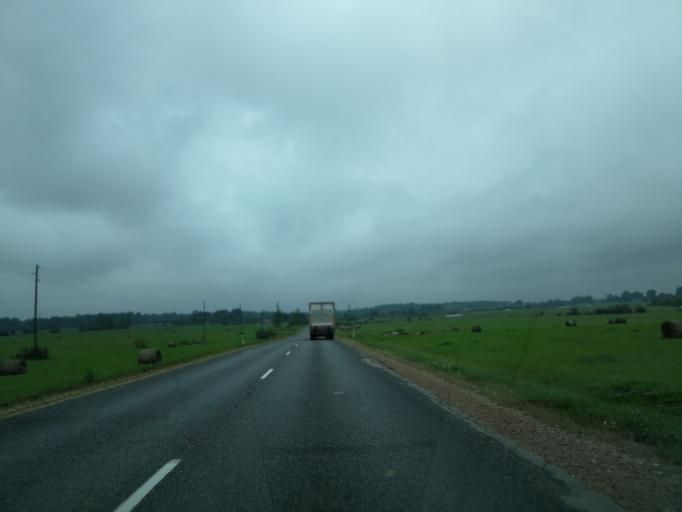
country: LV
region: Livani
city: Livani
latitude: 56.3545
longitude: 26.2392
